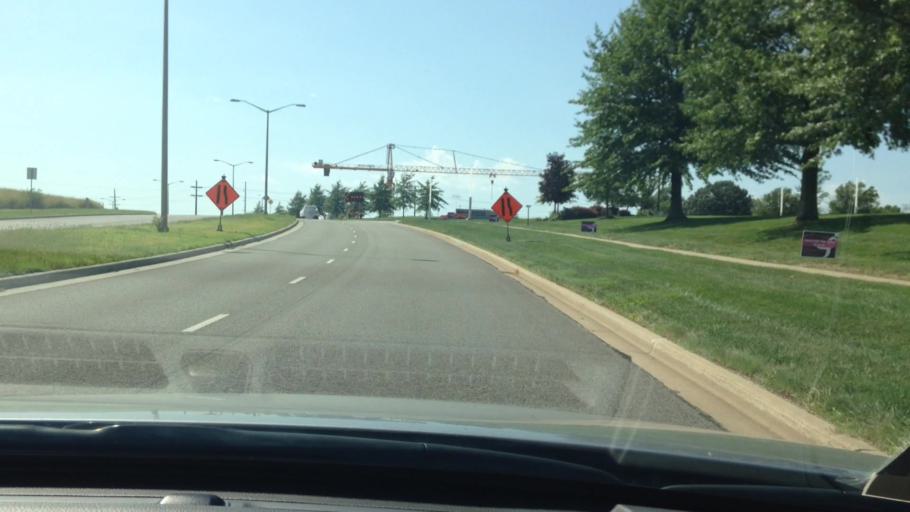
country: US
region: Kansas
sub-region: Johnson County
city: Leawood
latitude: 38.9223
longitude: -94.6550
